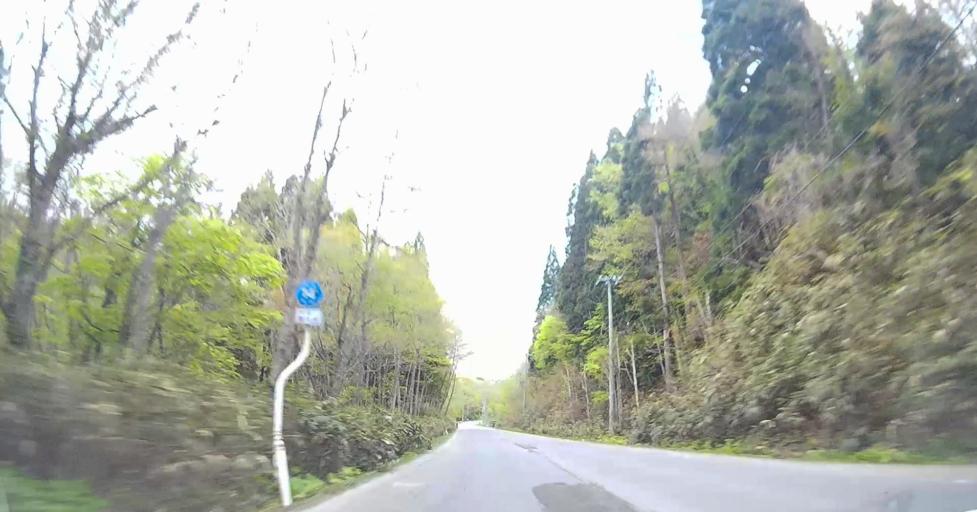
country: JP
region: Aomori
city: Goshogawara
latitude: 41.1134
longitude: 140.5303
